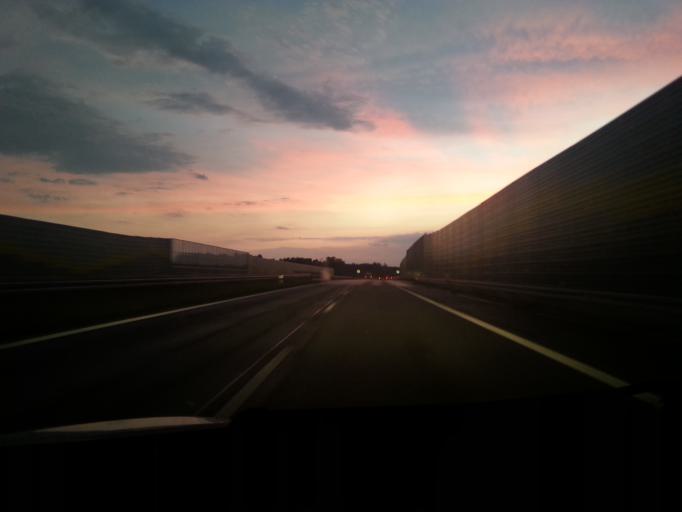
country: PL
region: Lodz Voivodeship
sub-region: Powiat zdunskowolski
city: Zdunska Wola
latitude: 51.5795
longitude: 18.9121
